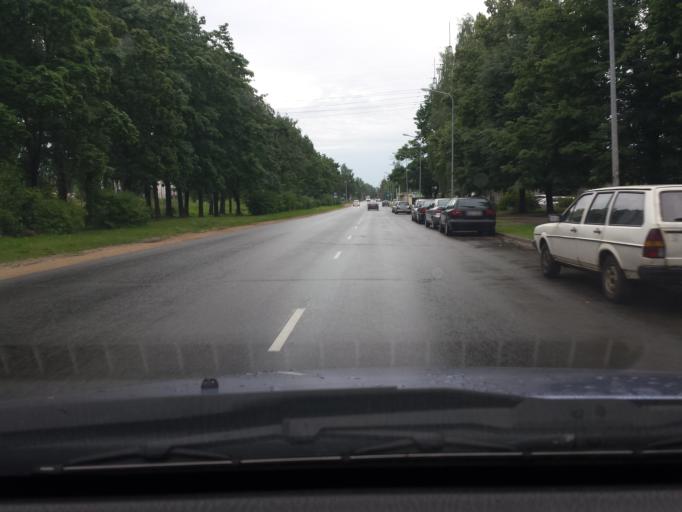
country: LV
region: Kekava
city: Kekava
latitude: 56.9061
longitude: 24.2071
